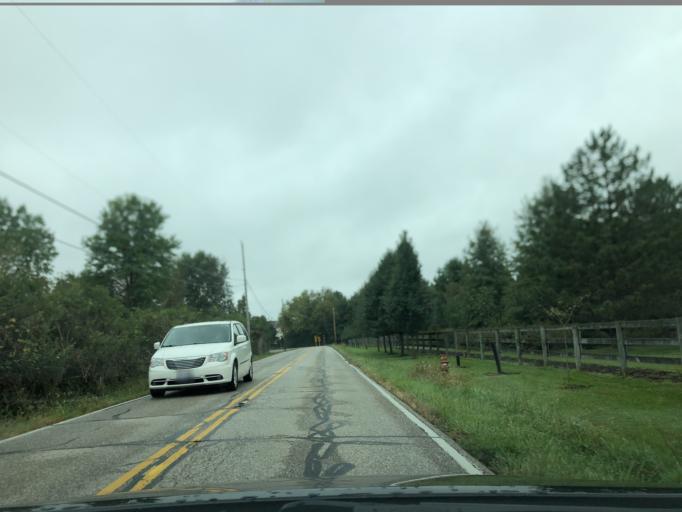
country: US
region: Ohio
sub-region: Hamilton County
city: Loveland
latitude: 39.2459
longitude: -84.2356
